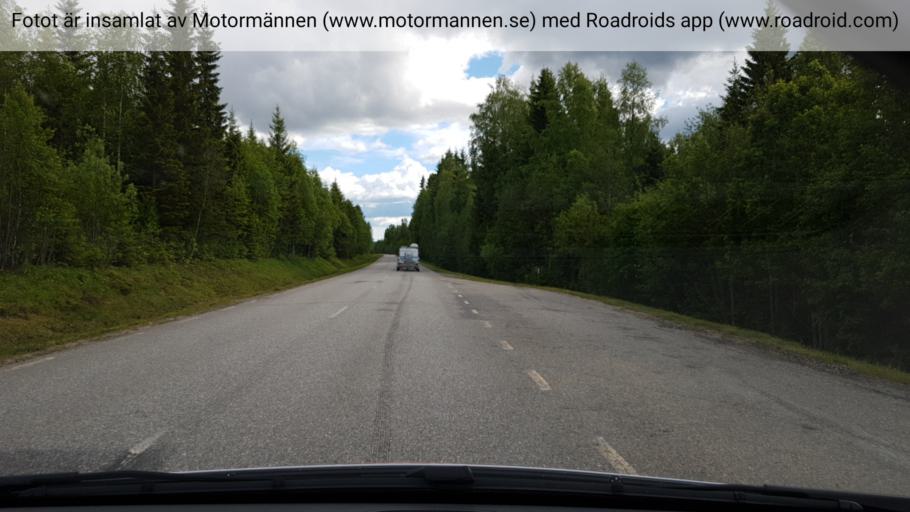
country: SE
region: Vaesterbotten
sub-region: Vannas Kommun
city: Vannasby
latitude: 64.0614
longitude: 19.9348
